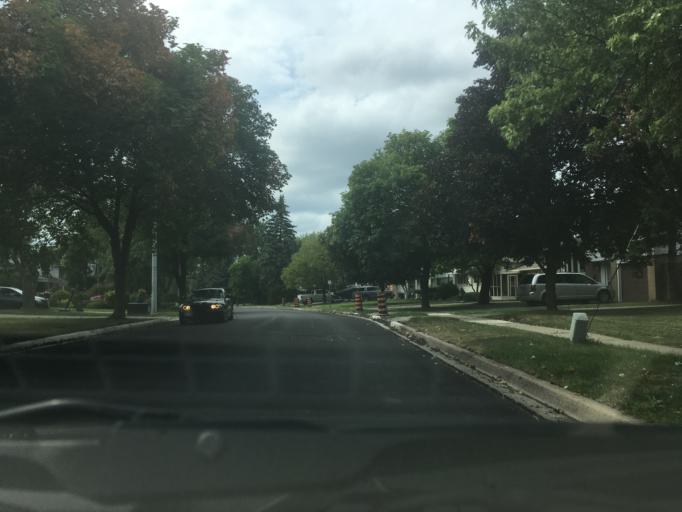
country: CA
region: Ontario
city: Brampton
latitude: 43.6727
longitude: -79.7348
